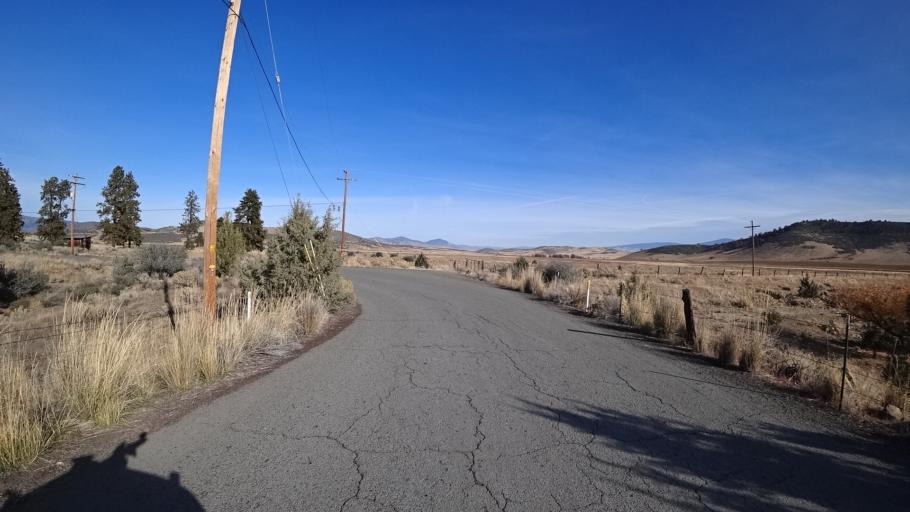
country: US
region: California
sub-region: Siskiyou County
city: Montague
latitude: 41.6360
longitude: -122.5685
